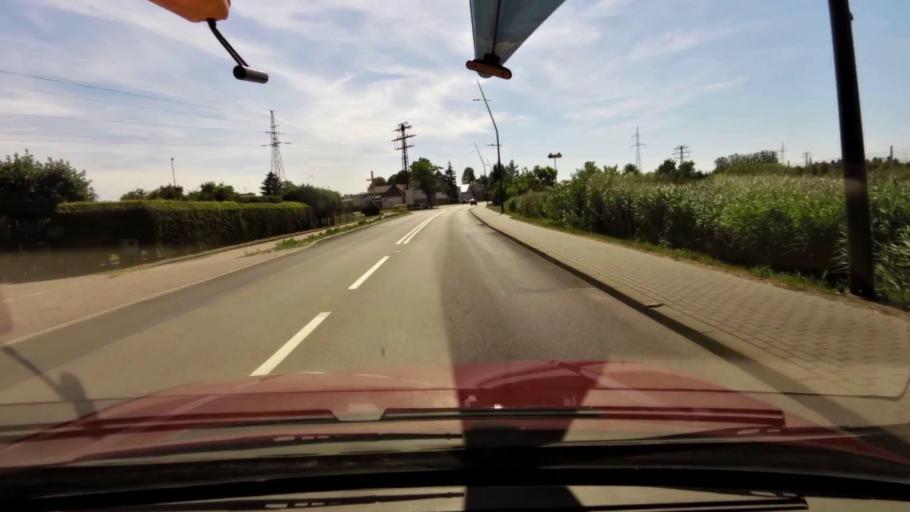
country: PL
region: Pomeranian Voivodeship
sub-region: Powiat slupski
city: Kobylnica
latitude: 54.4468
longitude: 17.0080
